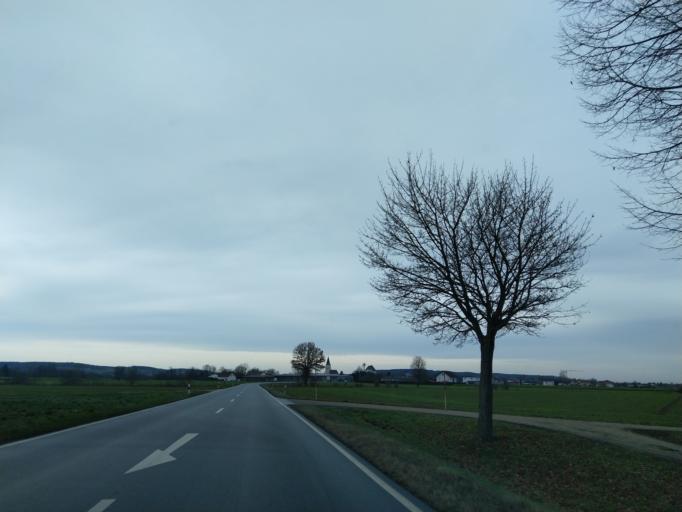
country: DE
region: Bavaria
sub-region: Lower Bavaria
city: Rossbach
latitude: 48.6185
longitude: 12.9977
